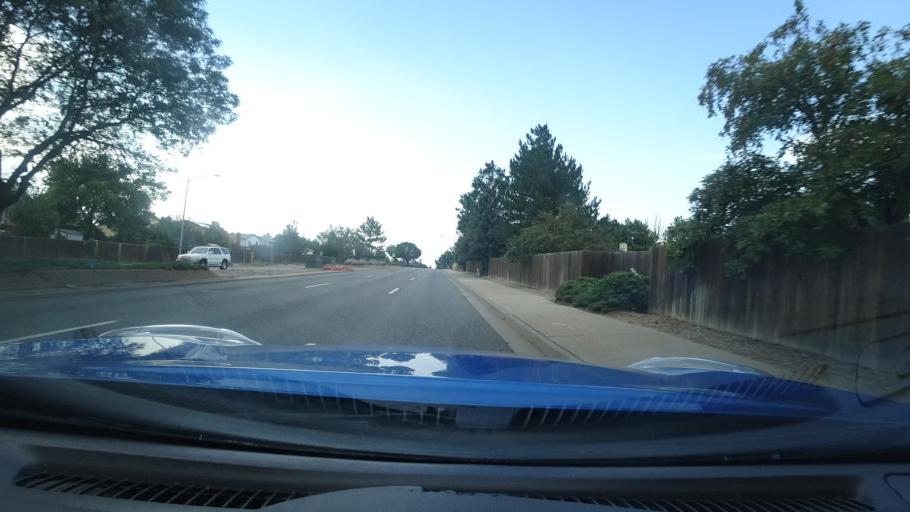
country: US
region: Colorado
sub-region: Adams County
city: Aurora
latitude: 39.6866
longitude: -104.8098
